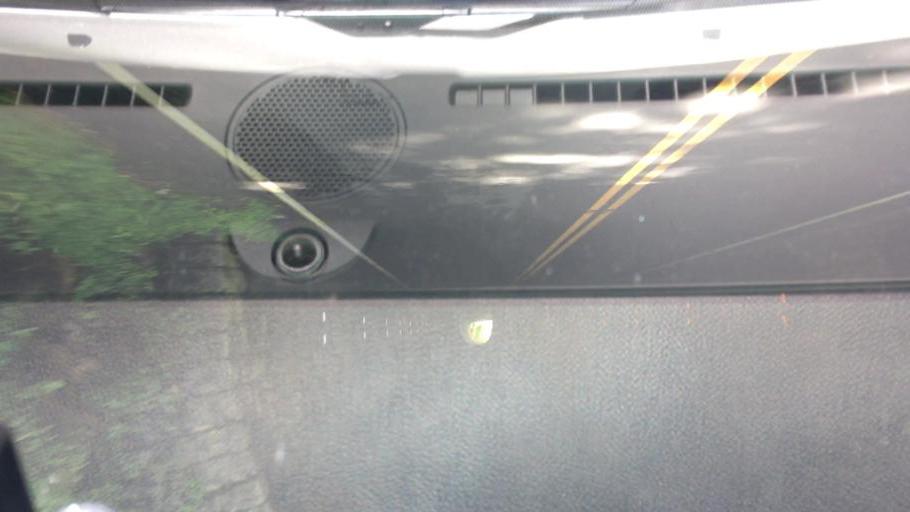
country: US
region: North Carolina
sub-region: Buncombe County
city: Swannanoa
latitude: 35.6653
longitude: -82.4617
